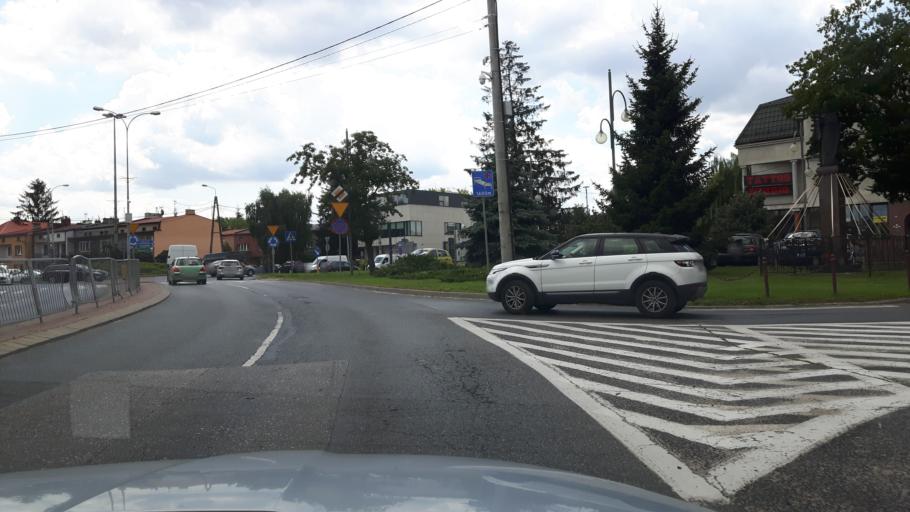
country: PL
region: Masovian Voivodeship
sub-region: Powiat wyszkowski
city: Wyszkow
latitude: 52.5934
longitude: 21.4584
